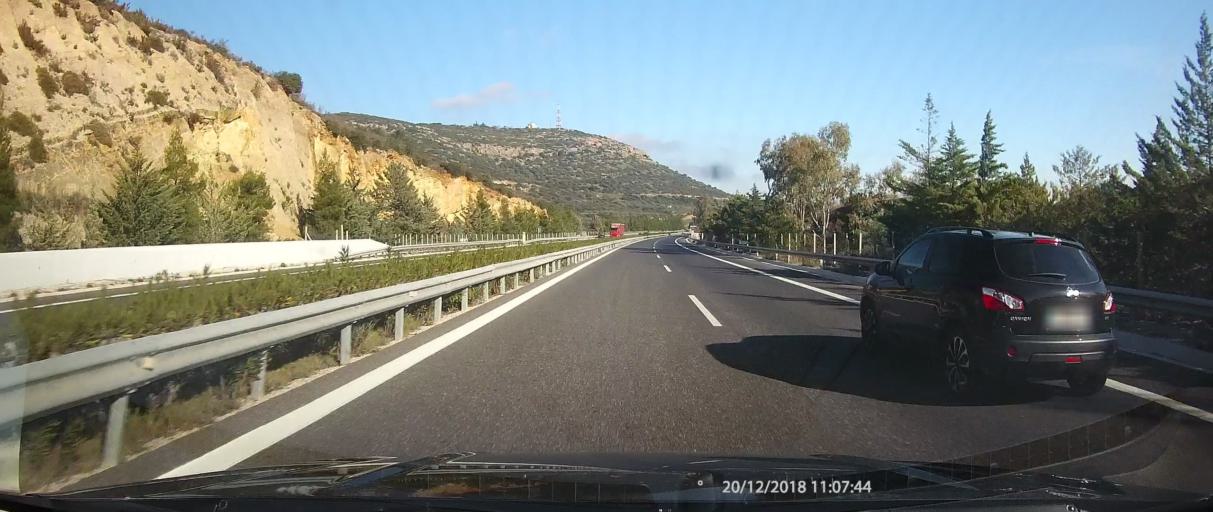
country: GR
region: Peloponnese
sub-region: Nomos Korinthias
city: Nemea
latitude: 37.7939
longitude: 22.7153
